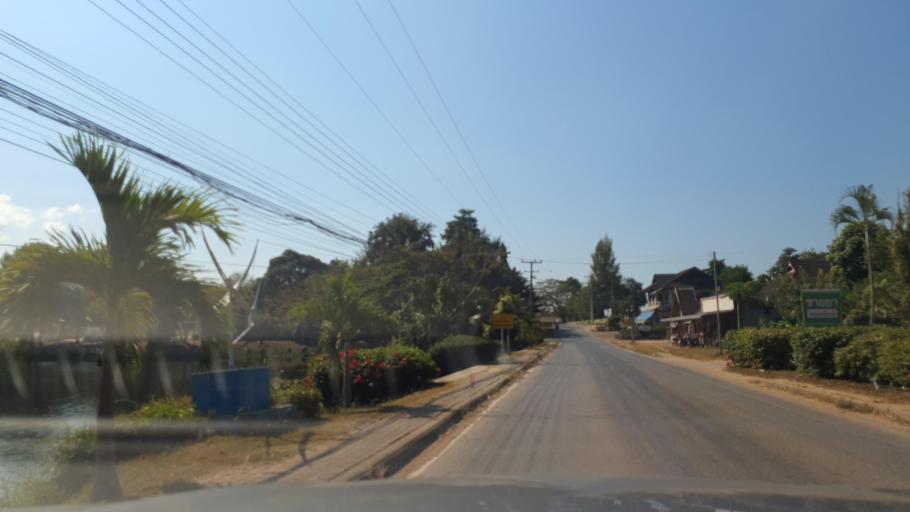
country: TH
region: Nan
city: Pua
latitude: 19.1375
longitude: 100.9326
